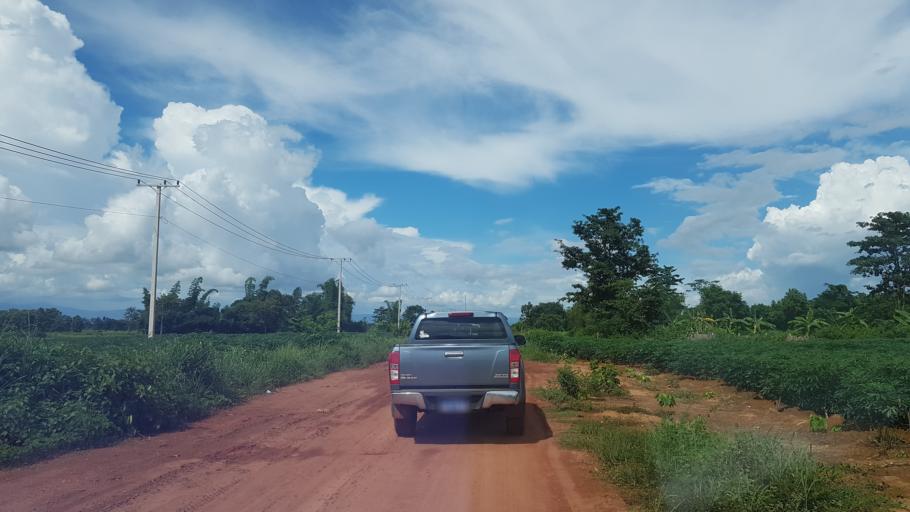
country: LA
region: Vientiane
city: Vientiane
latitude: 18.2050
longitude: 102.5693
